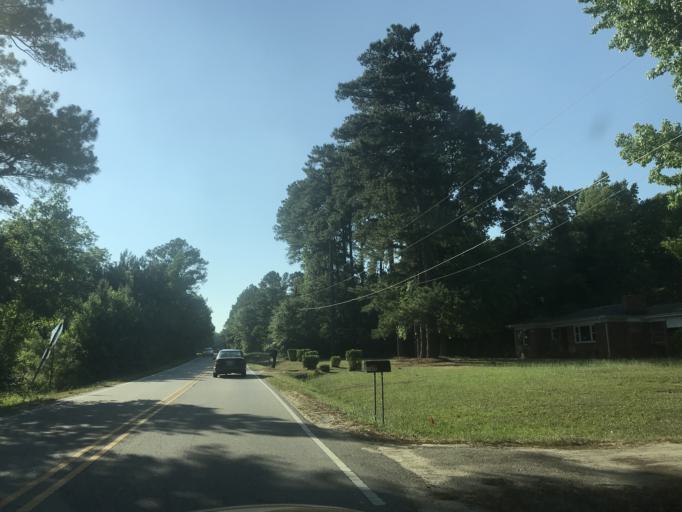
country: US
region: North Carolina
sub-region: Wake County
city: Garner
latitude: 35.7319
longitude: -78.6007
